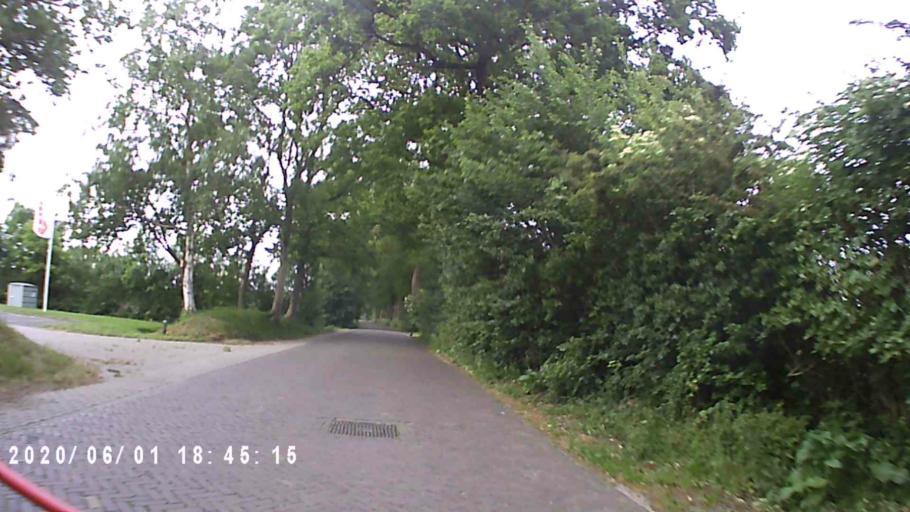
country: NL
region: Friesland
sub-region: Gemeente Tytsjerksteradiel
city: Eastermar
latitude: 53.1781
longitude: 6.0677
